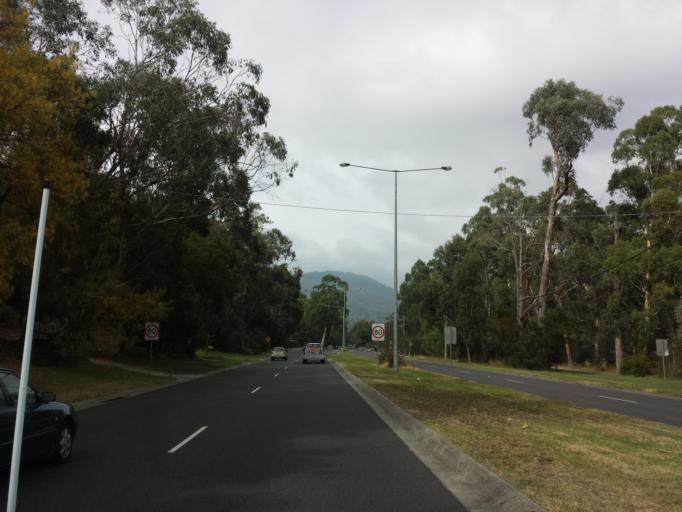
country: AU
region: Victoria
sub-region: Yarra Ranges
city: Mount Evelyn
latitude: -37.7902
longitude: 145.3612
